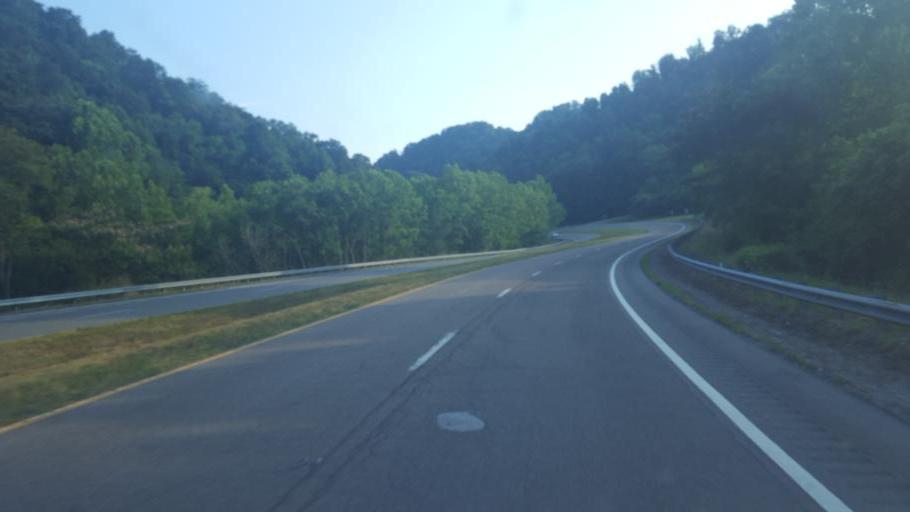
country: US
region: Tennessee
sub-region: Hawkins County
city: Mount Carmel
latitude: 36.6850
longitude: -82.7535
